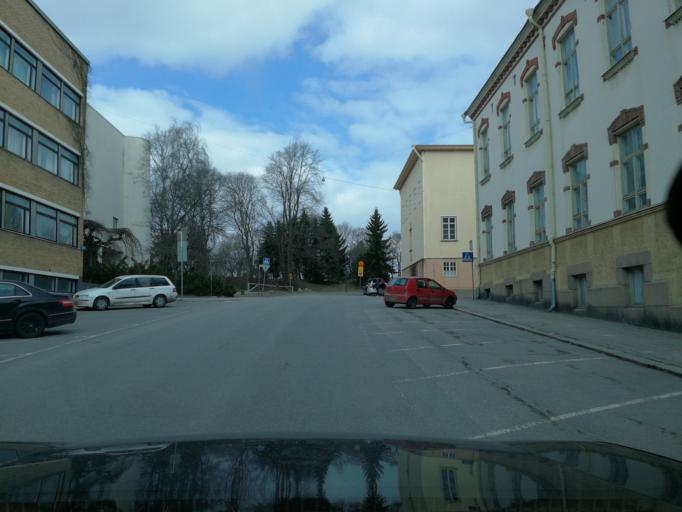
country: FI
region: Varsinais-Suomi
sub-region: Turku
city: Turku
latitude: 60.4442
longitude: 22.2693
